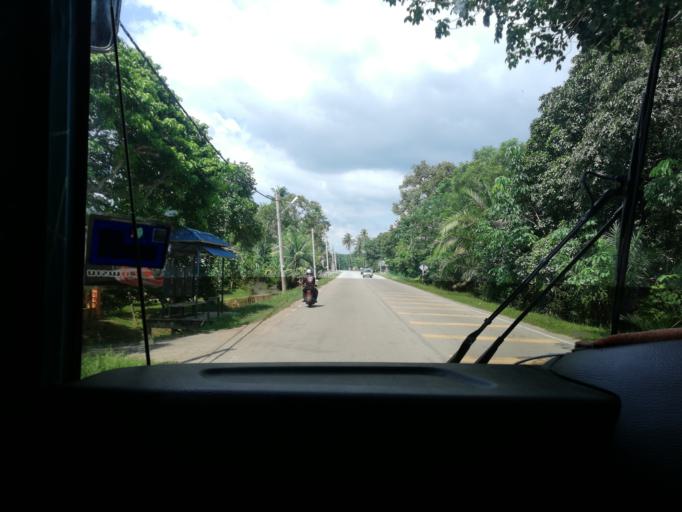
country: MY
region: Perak
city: Parit Buntar
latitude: 5.1167
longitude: 100.5599
